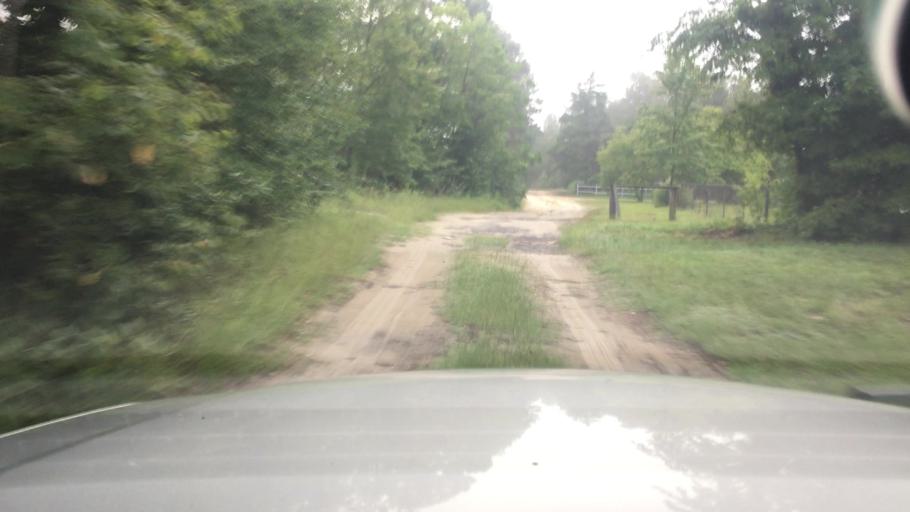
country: US
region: North Carolina
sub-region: Cumberland County
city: Hope Mills
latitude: 35.0199
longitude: -78.9385
